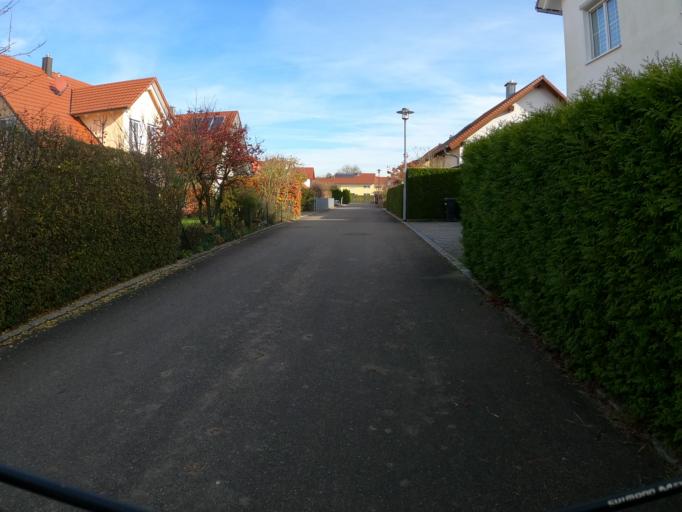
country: DE
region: Bavaria
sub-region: Swabia
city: Pfaffenhofen an der Roth
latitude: 48.4001
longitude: 10.1933
